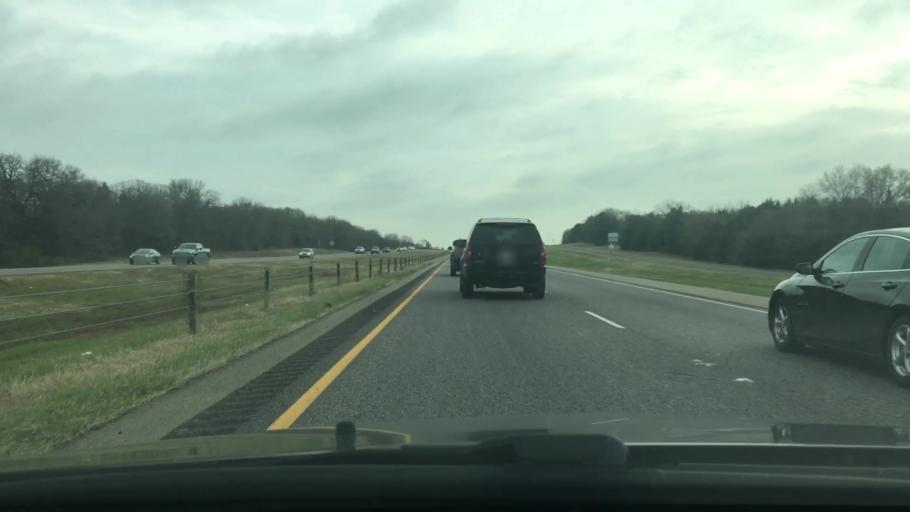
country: US
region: Texas
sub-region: Freestone County
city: Fairfield
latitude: 31.6452
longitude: -96.1593
